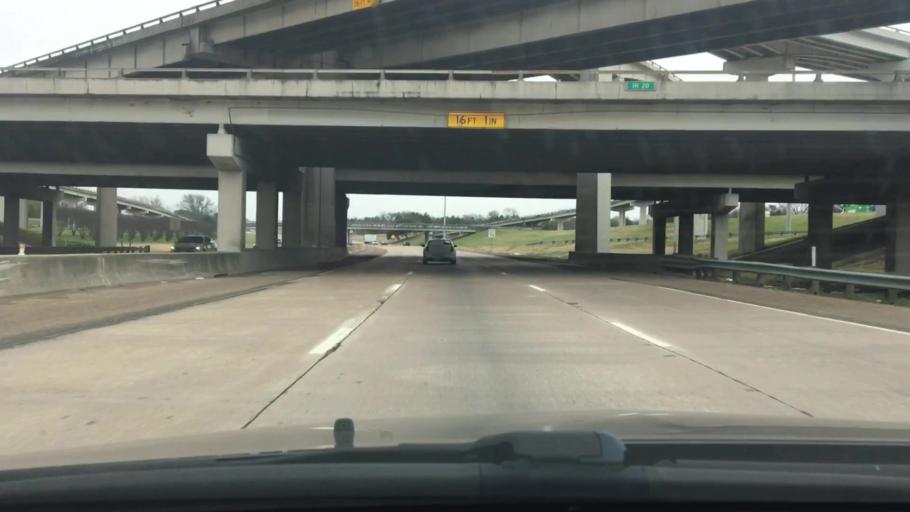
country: US
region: Texas
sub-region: Dallas County
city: Hutchins
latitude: 32.6620
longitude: -96.7269
